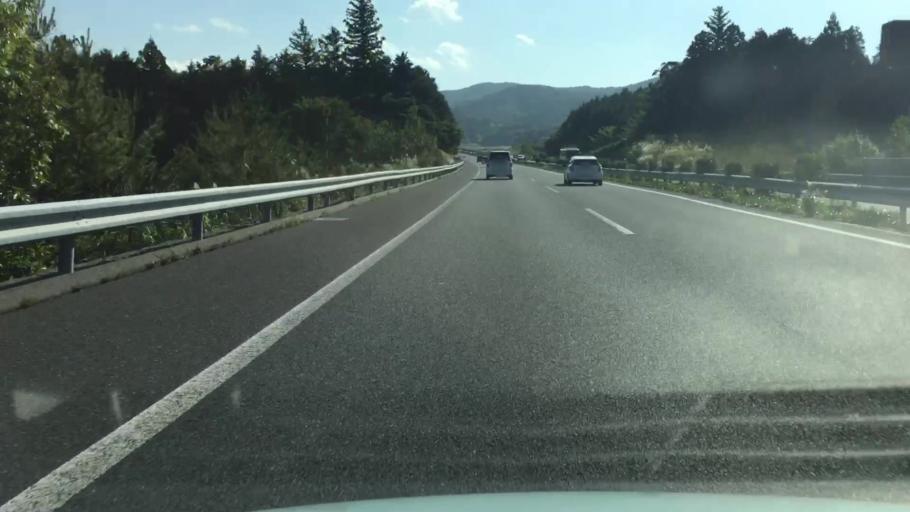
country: JP
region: Ibaraki
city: Iwase
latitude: 36.3440
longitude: 140.1804
